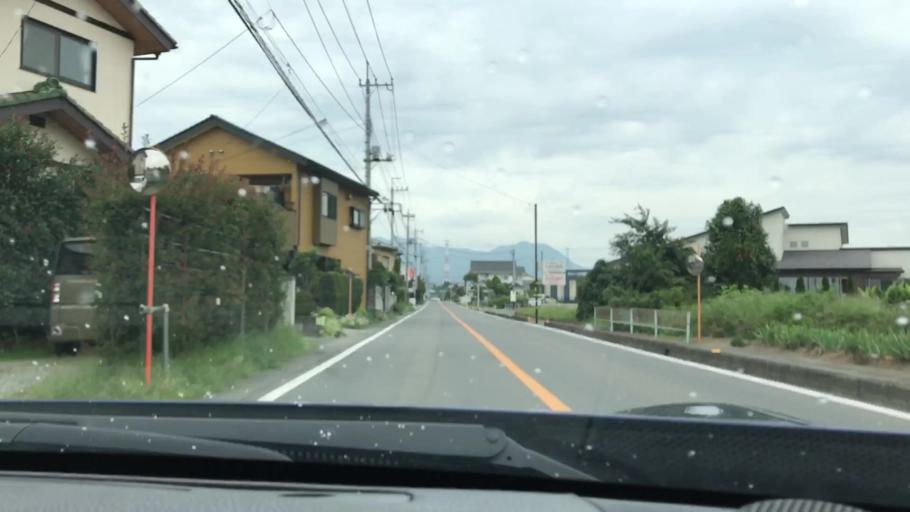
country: JP
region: Gunma
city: Kanekomachi
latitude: 36.3806
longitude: 138.9880
